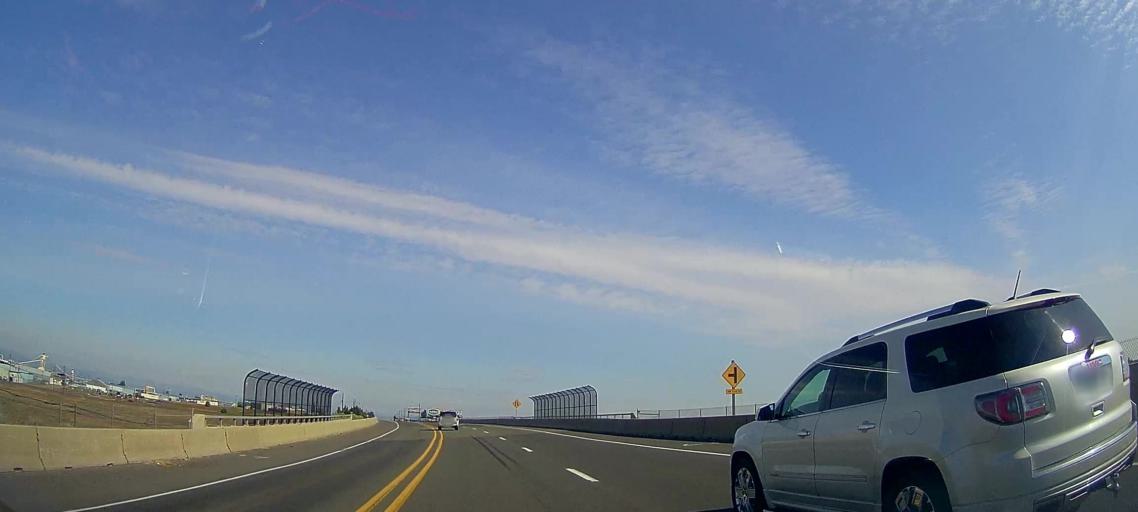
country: US
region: Oregon
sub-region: Jefferson County
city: Madras
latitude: 44.6553
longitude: -121.1290
